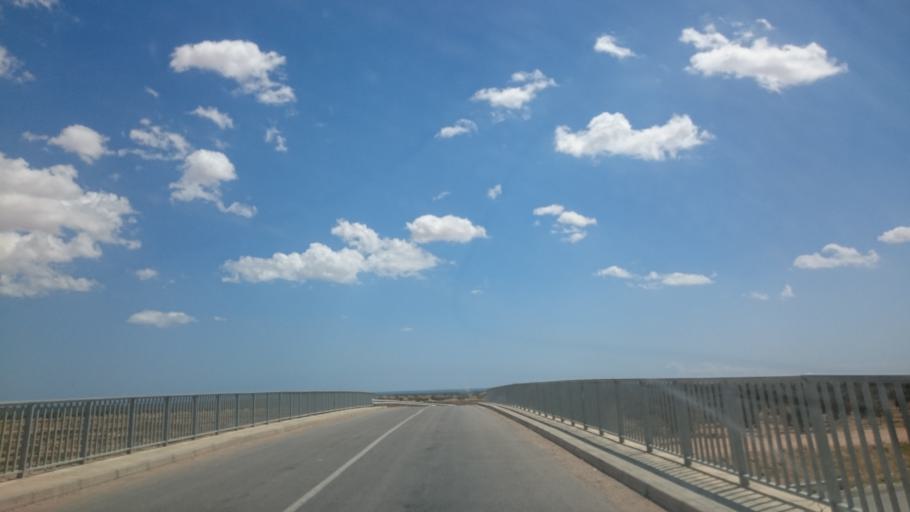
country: TN
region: Safaqis
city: Sfax
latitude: 34.6972
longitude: 10.5579
